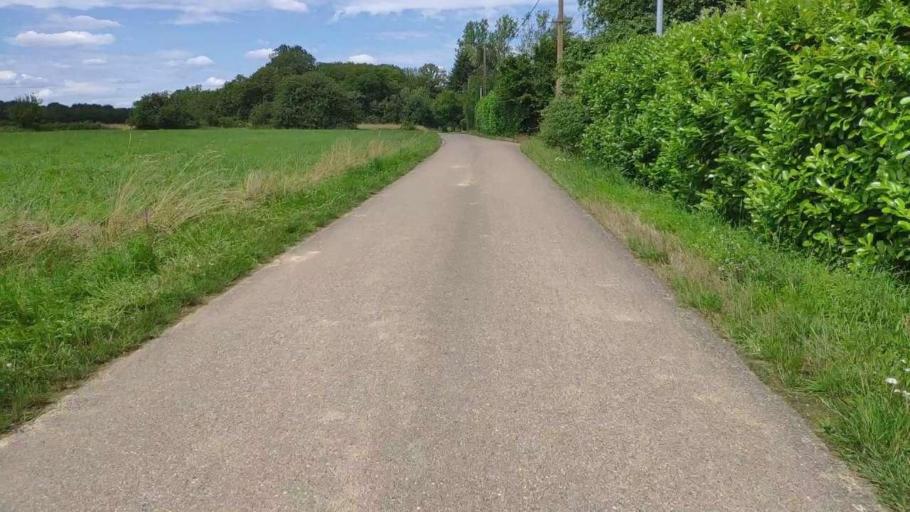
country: FR
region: Franche-Comte
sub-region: Departement du Jura
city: Chaussin
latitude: 46.8817
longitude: 5.4020
